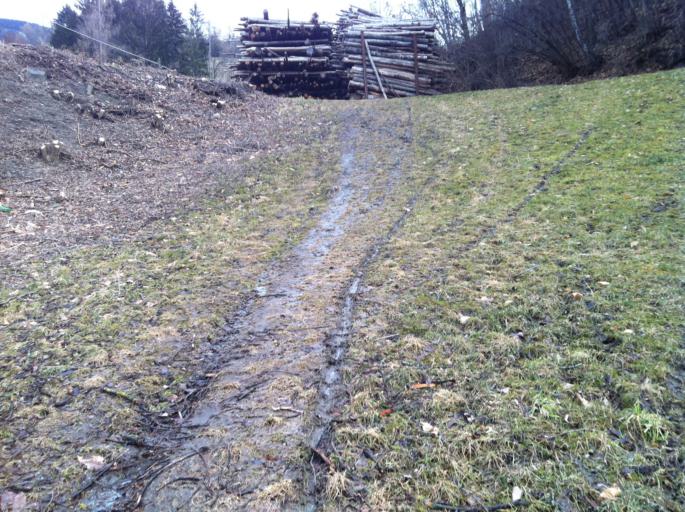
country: IT
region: Trentino-Alto Adige
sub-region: Bolzano
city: Bressanone
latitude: 46.6909
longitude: 11.6621
